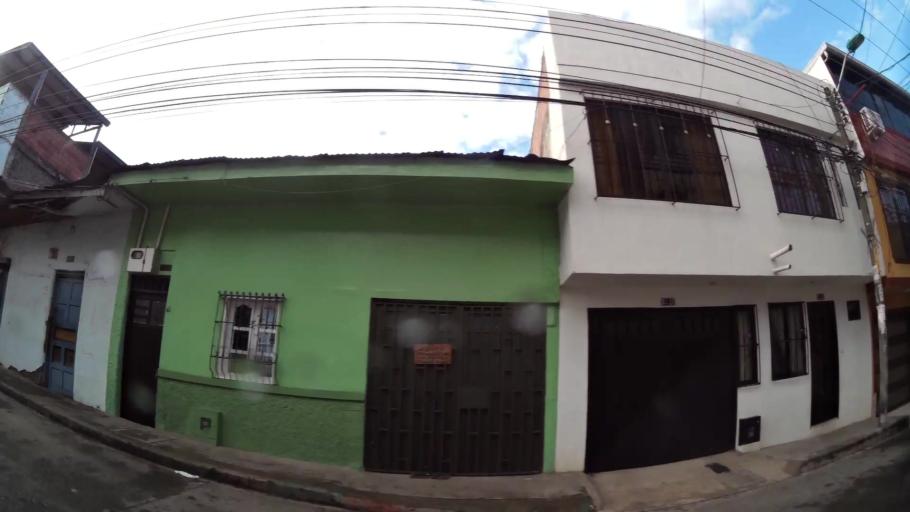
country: CO
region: Valle del Cauca
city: Cali
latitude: 3.4419
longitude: -76.5382
